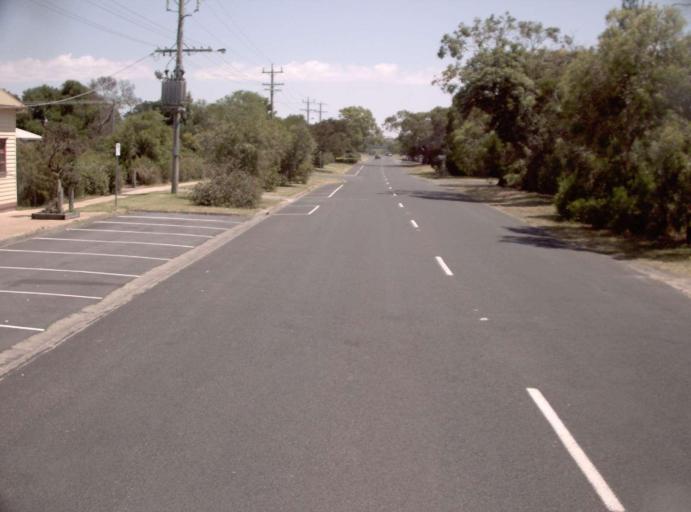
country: AU
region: Victoria
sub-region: Bass Coast
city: North Wonthaggi
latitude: -38.6992
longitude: 145.8674
